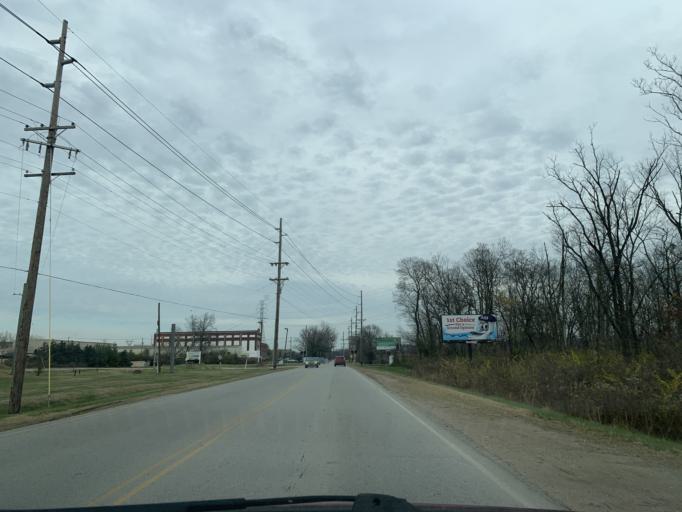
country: US
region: Indiana
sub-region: Clark County
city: Jeffersonville
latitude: 38.2679
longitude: -85.7165
